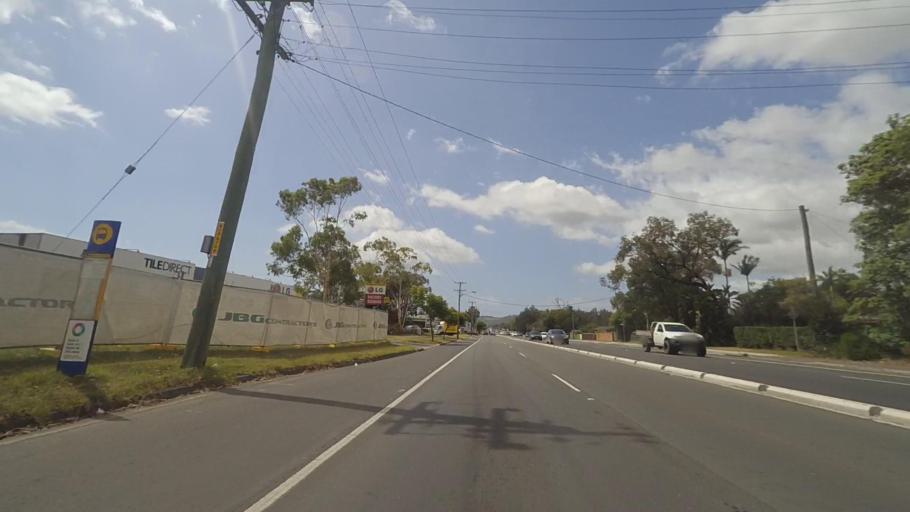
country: AU
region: New South Wales
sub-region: Shellharbour
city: Albion Park Rail
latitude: -34.5537
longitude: 150.7895
